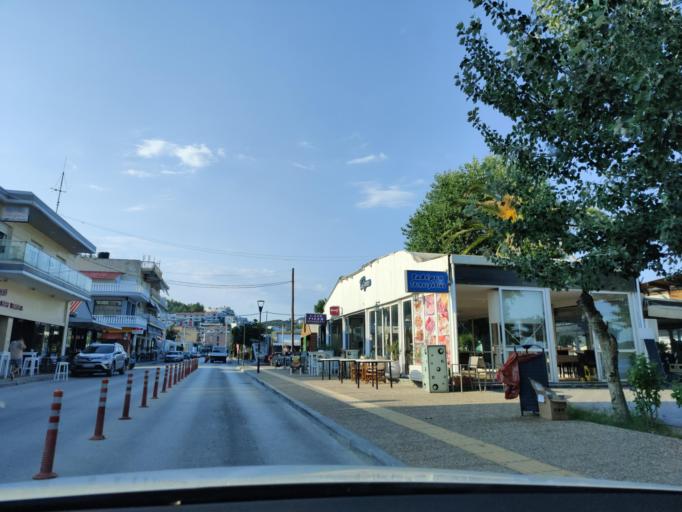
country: GR
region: East Macedonia and Thrace
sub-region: Nomos Kavalas
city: Nea Peramos
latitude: 40.8392
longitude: 24.3050
